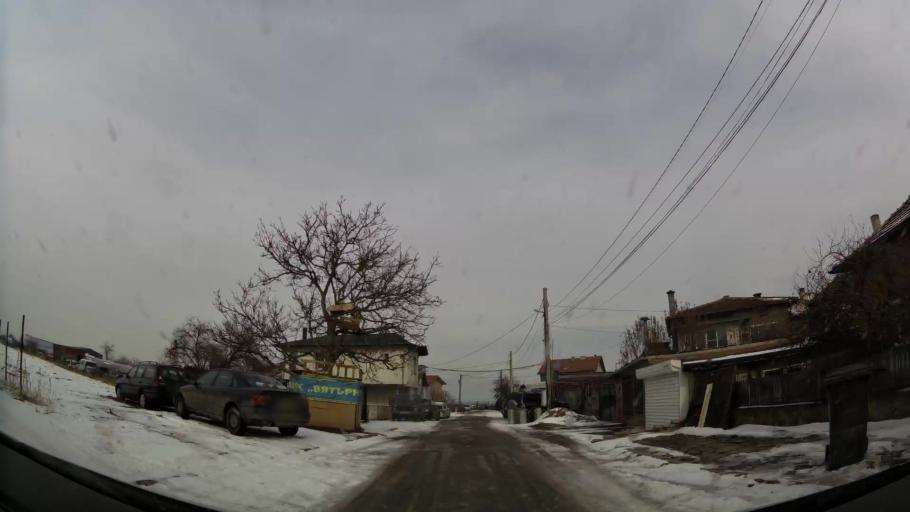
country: BG
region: Sofia-Capital
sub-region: Stolichna Obshtina
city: Sofia
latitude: 42.7149
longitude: 23.4001
